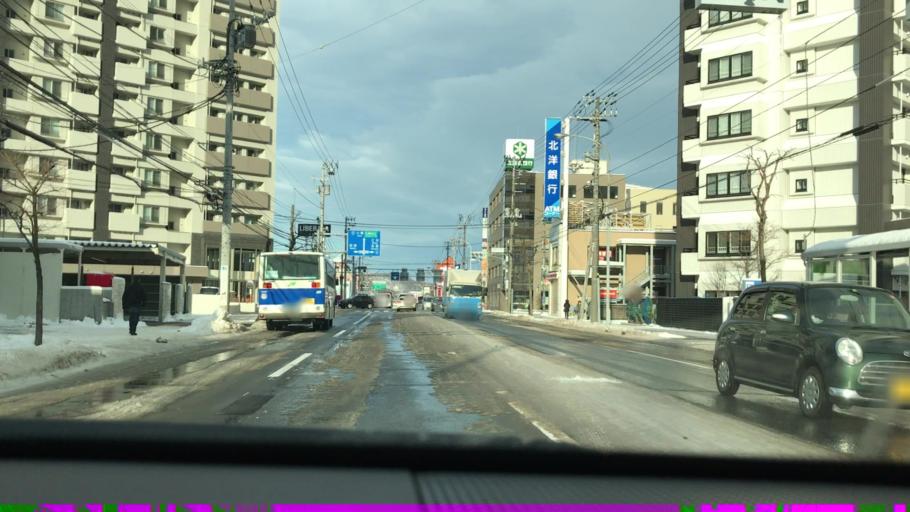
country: JP
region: Hokkaido
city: Sapporo
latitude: 43.0868
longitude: 141.2757
